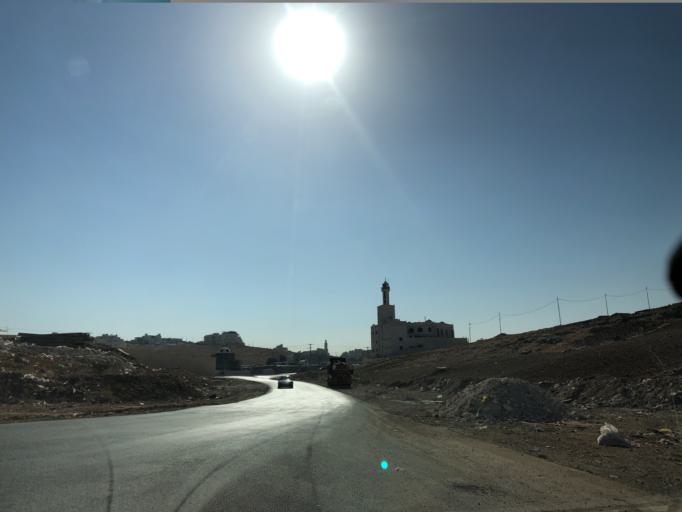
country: JO
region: Amman
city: Wadi as Sir
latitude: 31.9347
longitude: 35.8428
